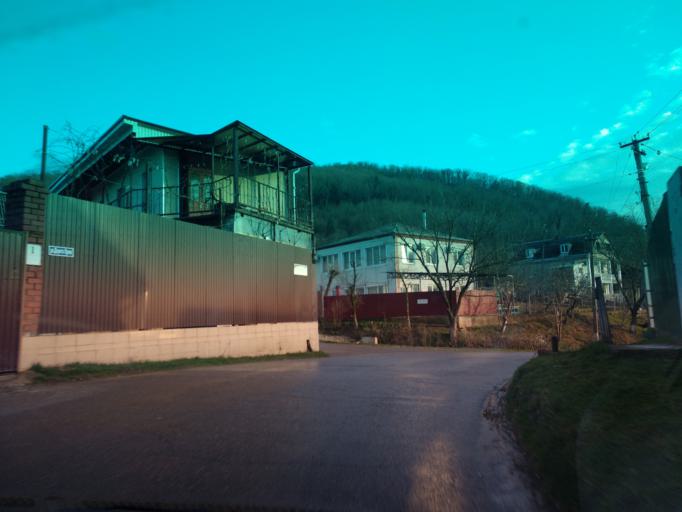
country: RU
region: Krasnodarskiy
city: Novomikhaylovskiy
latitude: 44.2697
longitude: 38.8306
